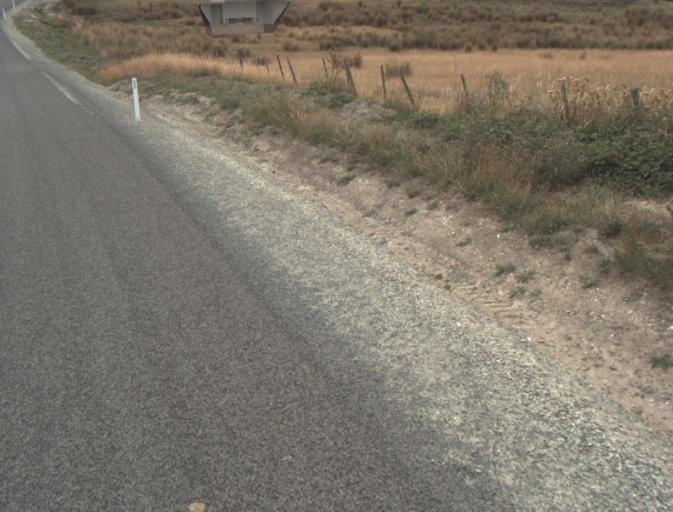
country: AU
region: Tasmania
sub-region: Launceston
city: Mayfield
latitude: -41.1932
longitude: 147.1725
